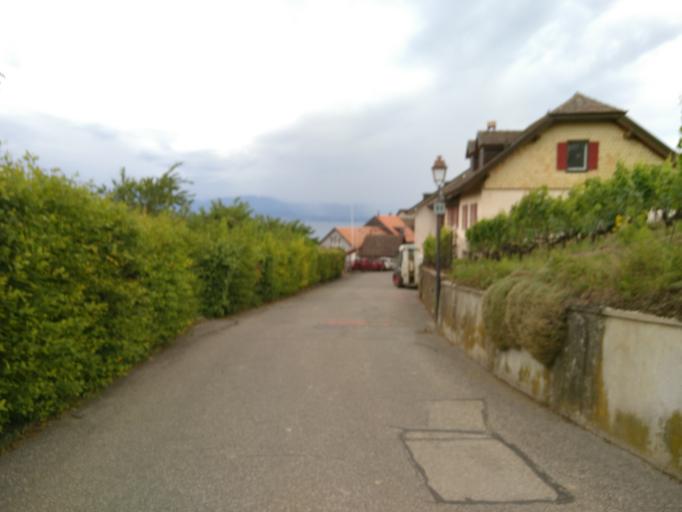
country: CH
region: Vaud
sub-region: Nyon District
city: Perroy
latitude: 46.4827
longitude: 6.3703
